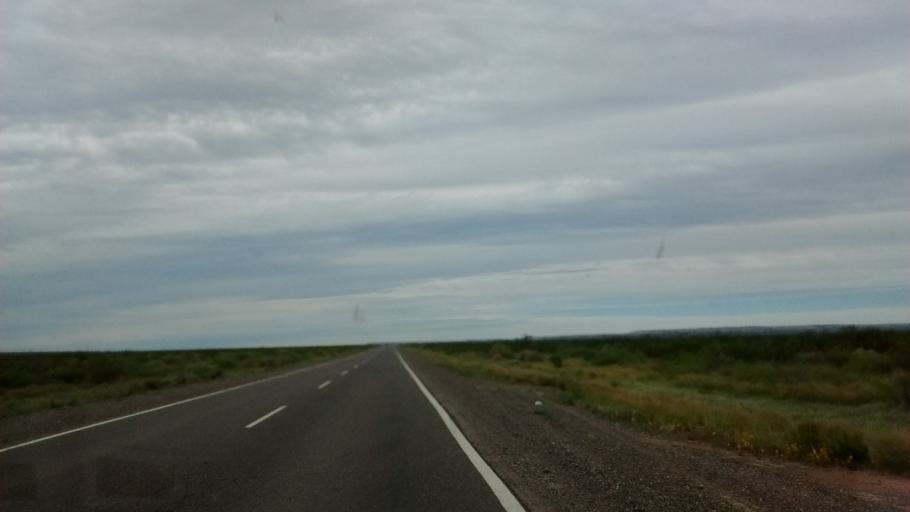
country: AR
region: Rio Negro
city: Catriel
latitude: -38.0682
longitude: -67.9227
